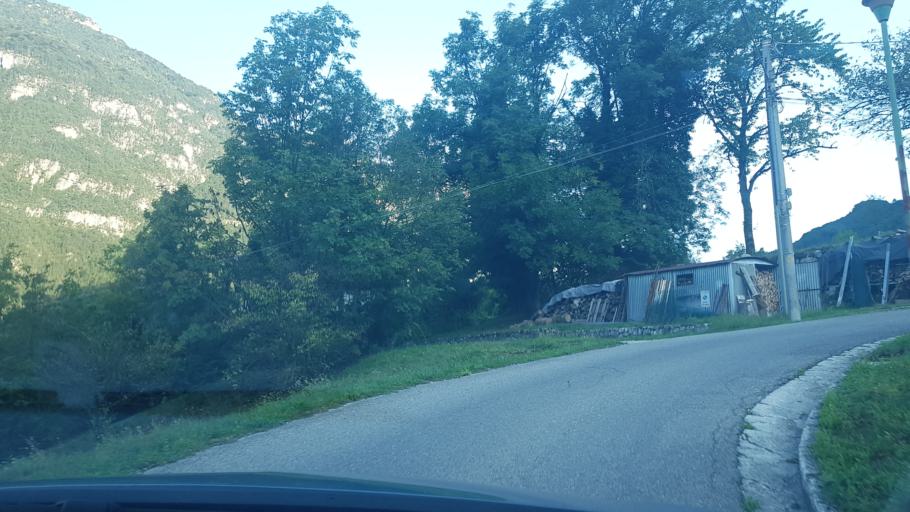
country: IT
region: Friuli Venezia Giulia
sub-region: Provincia di Udine
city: Moggio Udinese
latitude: 46.4274
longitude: 13.2056
